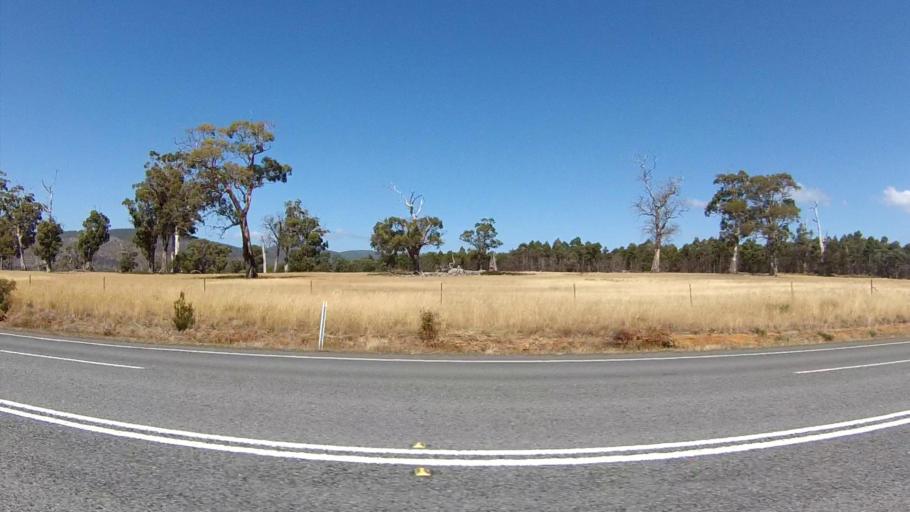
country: AU
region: Tasmania
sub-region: Sorell
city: Sorell
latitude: -42.5992
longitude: 147.7624
